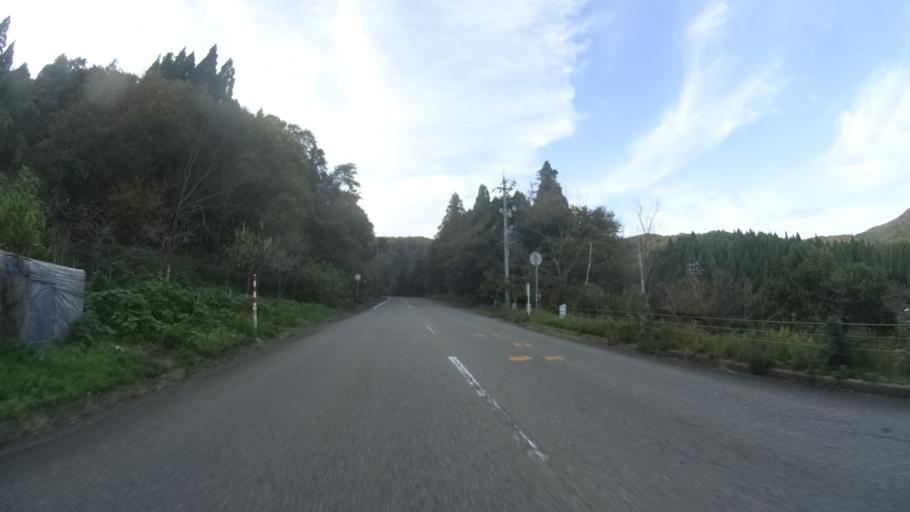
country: JP
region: Ishikawa
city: Nanao
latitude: 37.1979
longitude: 136.7129
